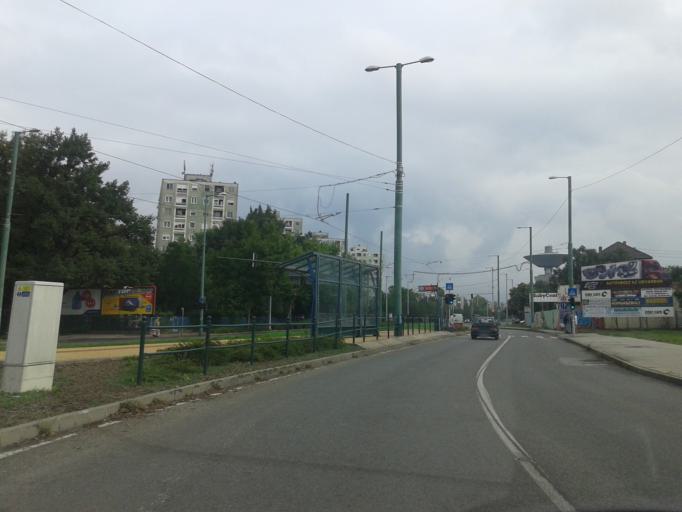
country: HU
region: Csongrad
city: Szeged
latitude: 46.2646
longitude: 20.1311
